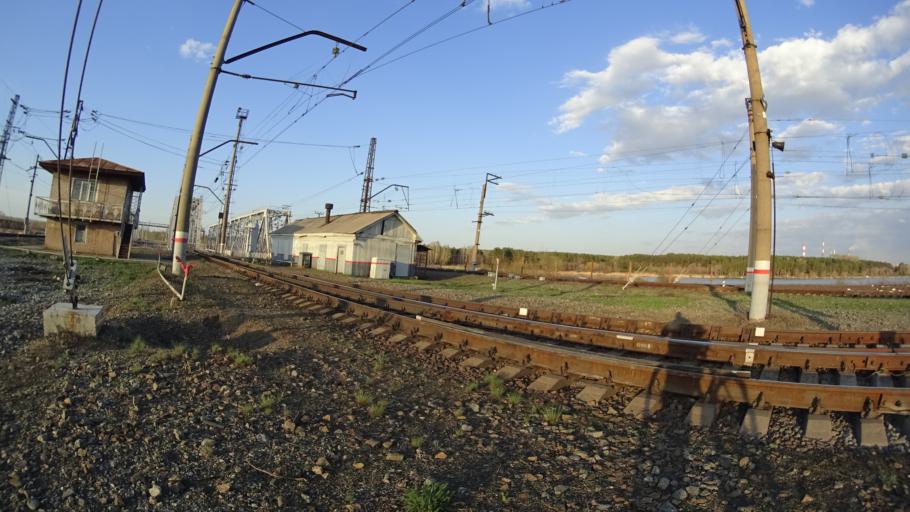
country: RU
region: Chelyabinsk
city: Troitsk
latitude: 54.0544
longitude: 61.6101
